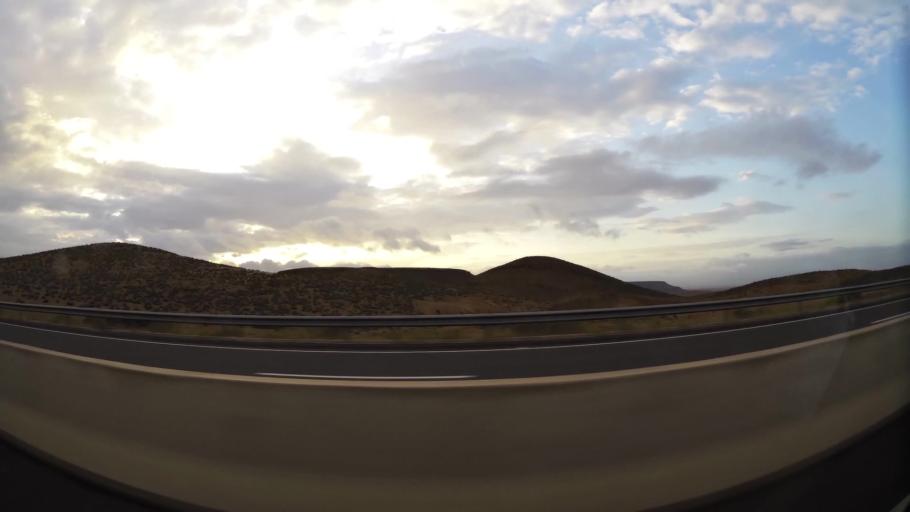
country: MA
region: Oriental
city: Taourirt
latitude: 34.4665
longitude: -3.0393
